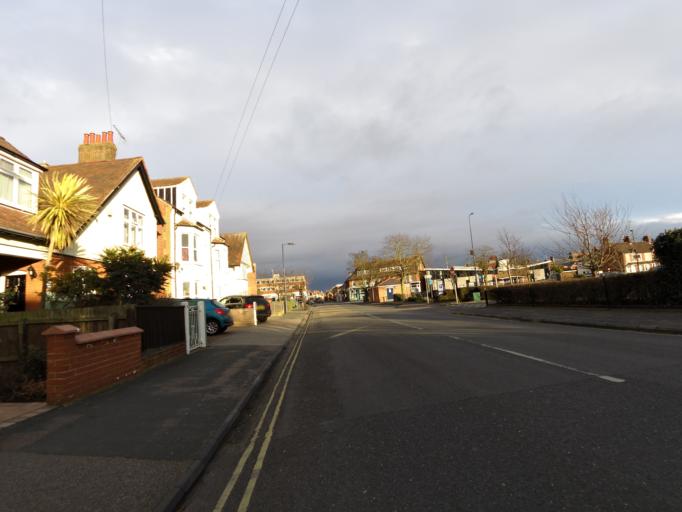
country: GB
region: England
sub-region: Suffolk
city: Felixstowe
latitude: 51.9640
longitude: 1.3498
